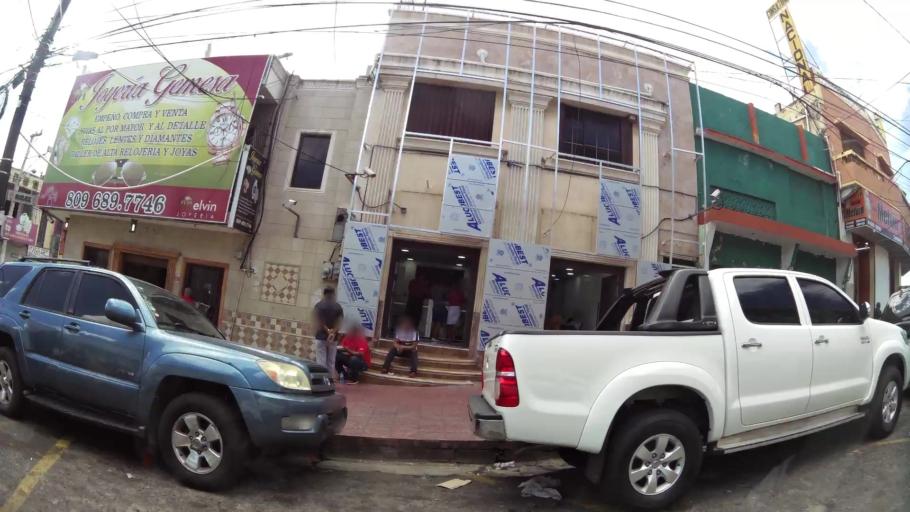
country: DO
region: Nacional
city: San Carlos
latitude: 18.4841
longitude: -69.8944
